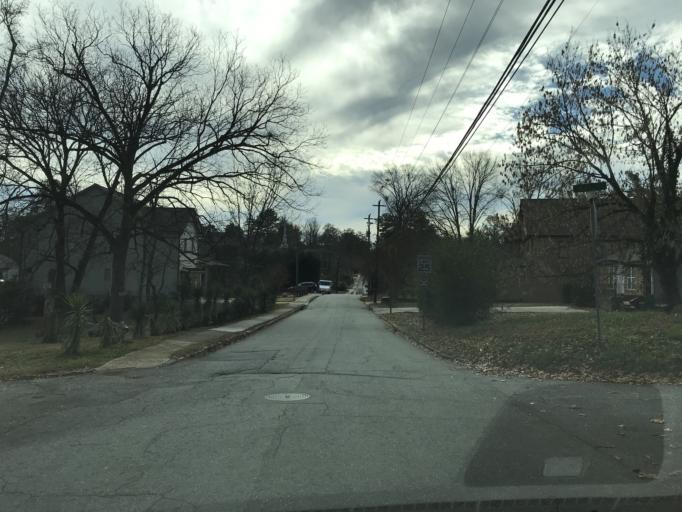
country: US
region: Georgia
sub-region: DeKalb County
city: North Atlanta
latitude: 33.8835
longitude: -84.3423
